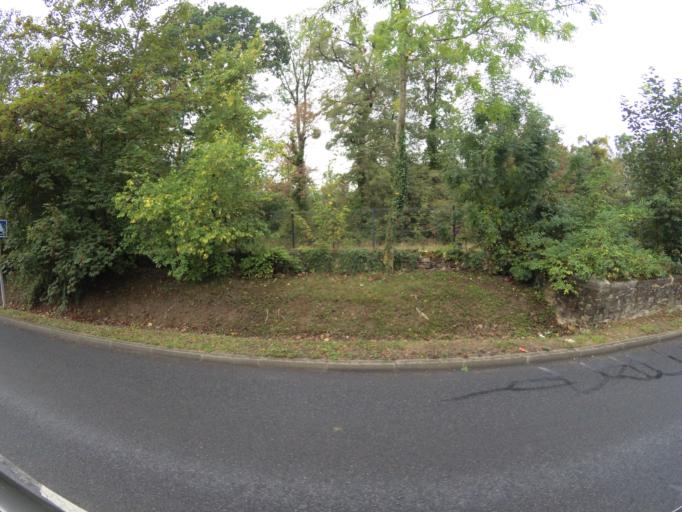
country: FR
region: Ile-de-France
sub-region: Departement de Seine-et-Marne
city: Guermantes
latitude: 48.8510
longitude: 2.7041
